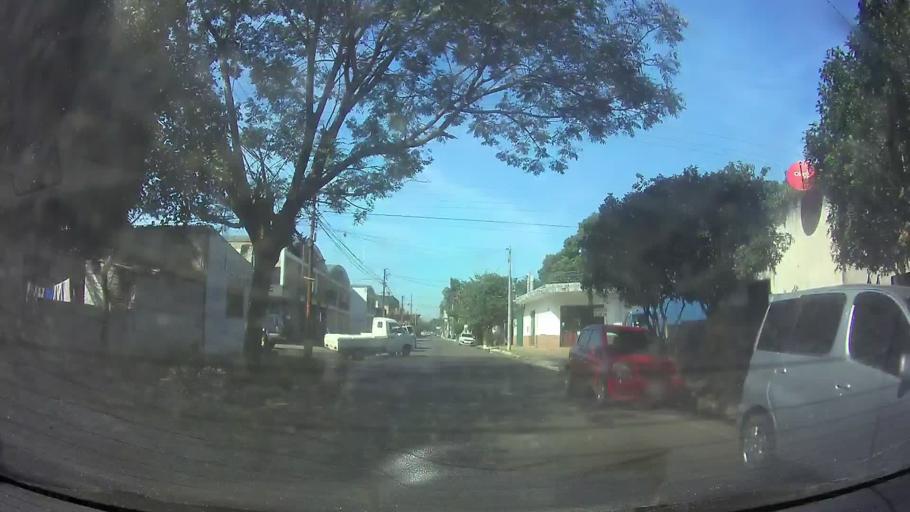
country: PY
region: Central
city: Fernando de la Mora
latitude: -25.3259
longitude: -57.5644
